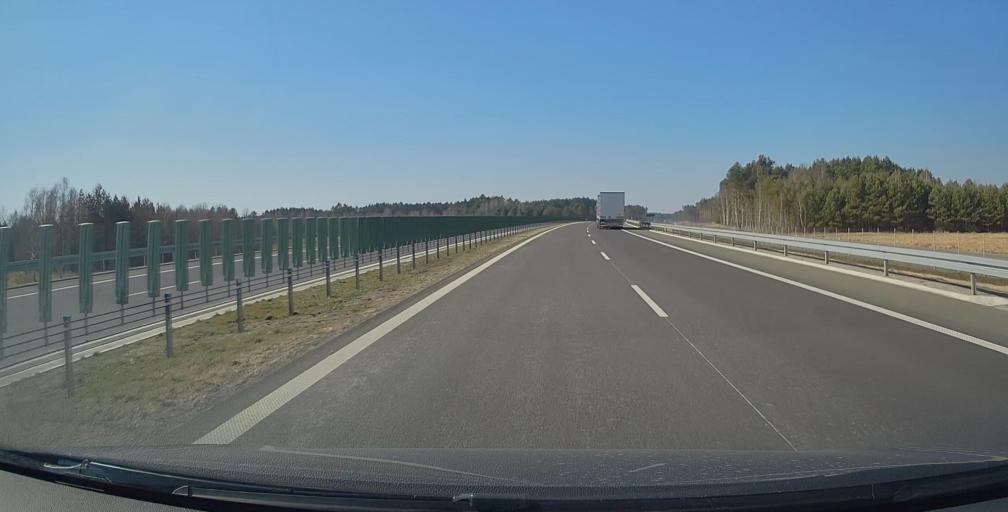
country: PL
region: Subcarpathian Voivodeship
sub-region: Powiat nizanski
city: Raclawice
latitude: 50.4756
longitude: 22.1757
